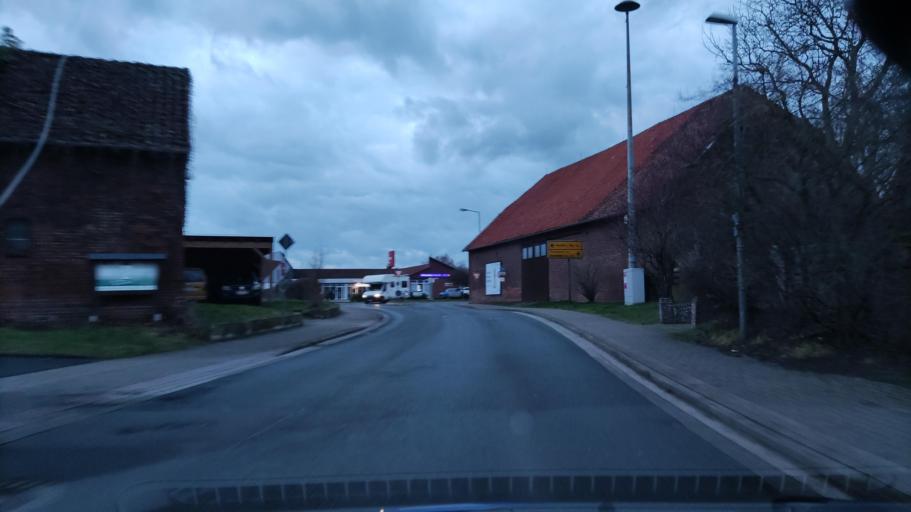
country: DE
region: Lower Saxony
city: Schwarmstedt
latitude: 52.5996
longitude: 9.5667
